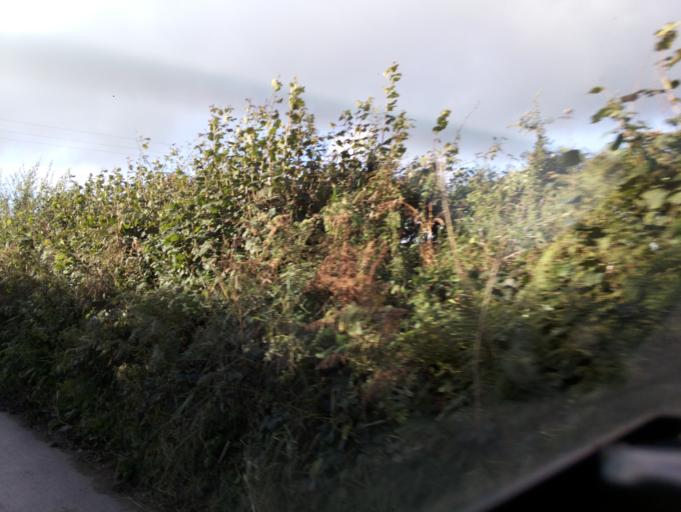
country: GB
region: England
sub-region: Devon
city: Totnes
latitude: 50.3633
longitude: -3.7372
